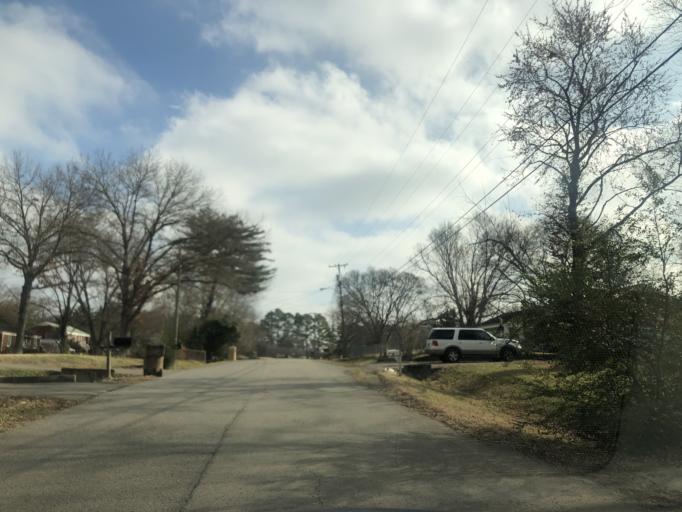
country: US
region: Tennessee
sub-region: Davidson County
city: Oak Hill
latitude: 36.0815
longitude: -86.6945
